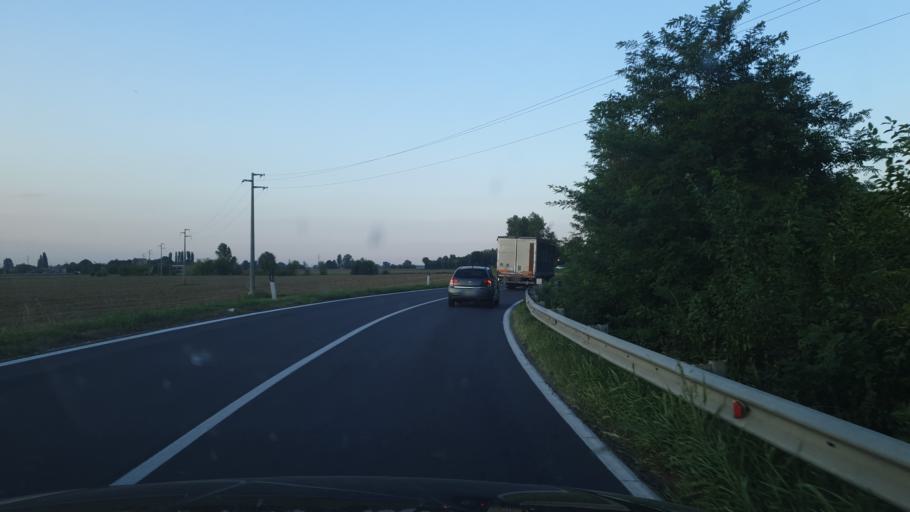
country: IT
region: Emilia-Romagna
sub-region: Provincia di Bologna
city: Progresso
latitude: 44.5554
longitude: 11.3903
